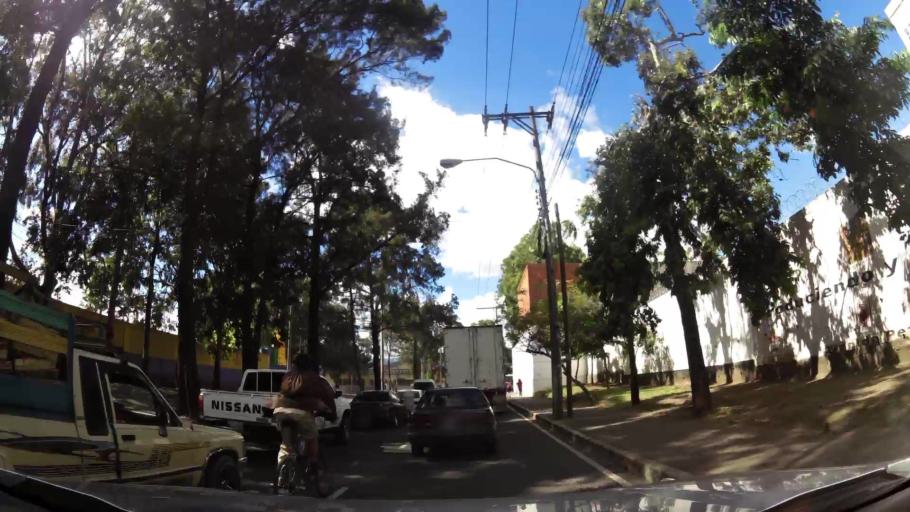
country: GT
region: Guatemala
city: Villa Nueva
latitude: 14.5576
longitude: -90.5508
